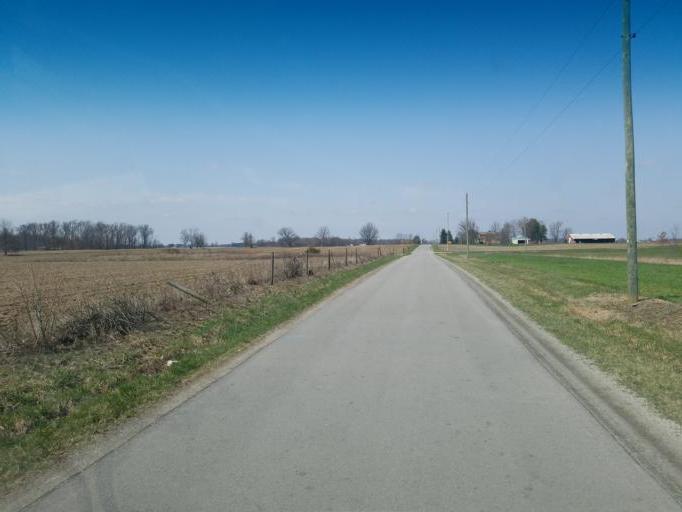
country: US
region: Ohio
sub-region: Wyandot County
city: Upper Sandusky
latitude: 40.8762
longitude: -83.3361
